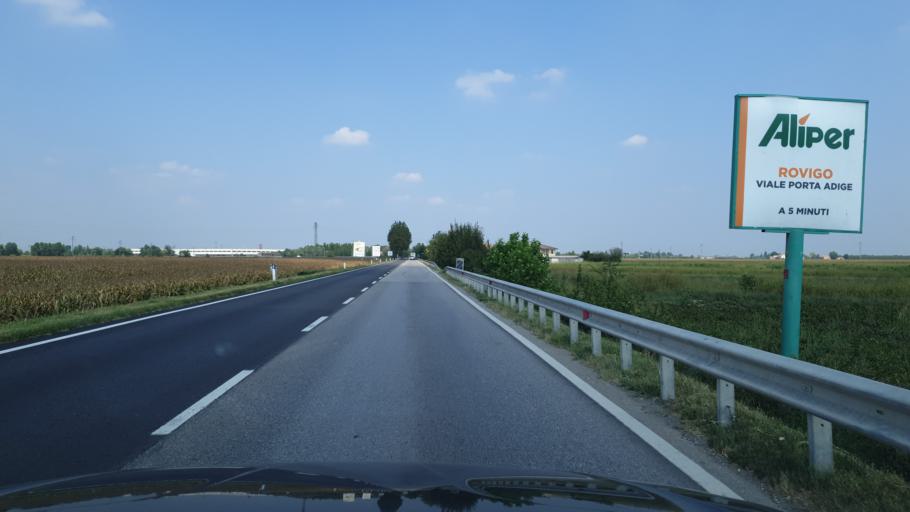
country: IT
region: Veneto
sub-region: Provincia di Rovigo
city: Bosaro
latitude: 45.0173
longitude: 11.7701
